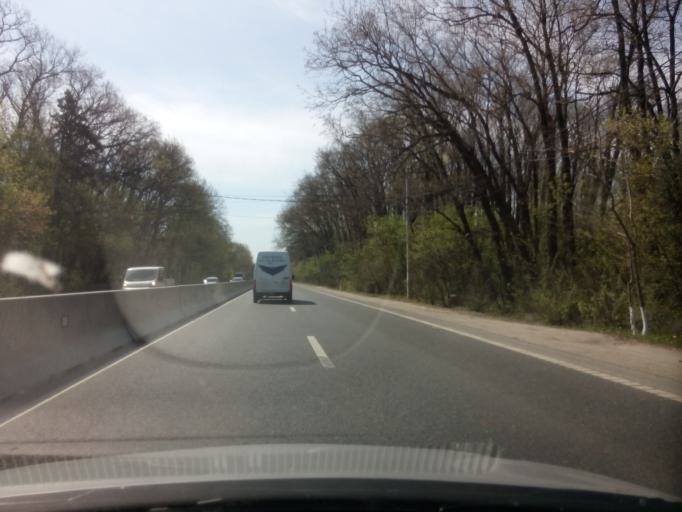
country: RO
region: Ilfov
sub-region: Comuna Corbeanca
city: Corbeanca
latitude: 44.5892
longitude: 26.0708
